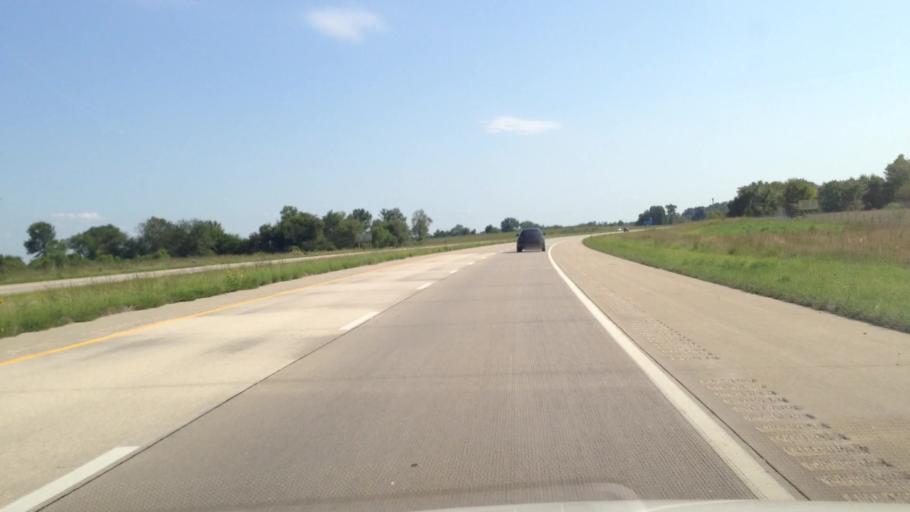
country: US
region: Kansas
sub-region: Linn County
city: Pleasanton
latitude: 38.2752
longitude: -94.6693
